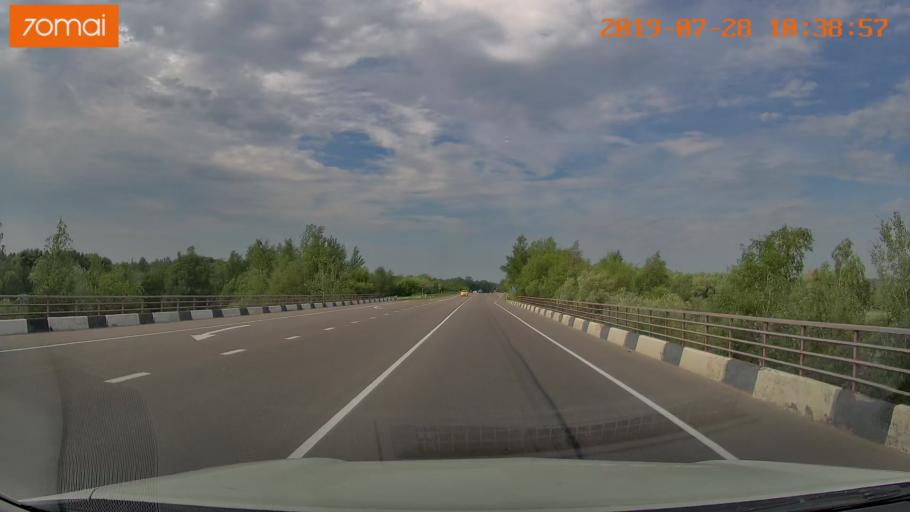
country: RU
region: Kaliningrad
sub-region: Gorod Kaliningrad
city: Kaliningrad
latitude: 54.7207
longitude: 20.3900
